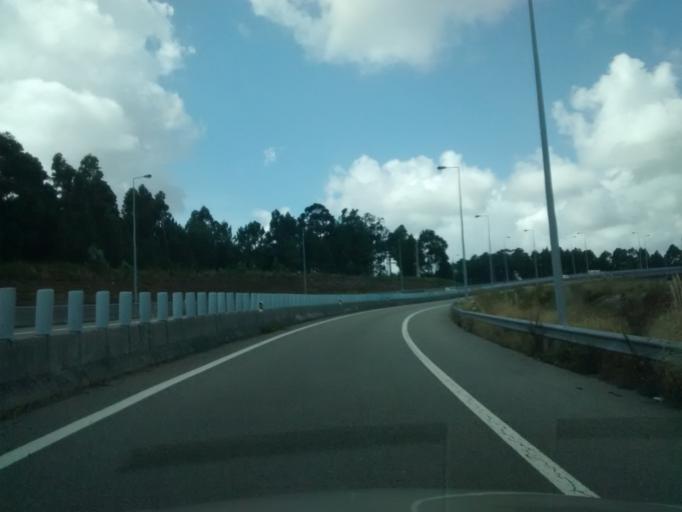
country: PT
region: Aveiro
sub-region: Aveiro
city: Eixo
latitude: 40.6432
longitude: -8.5979
